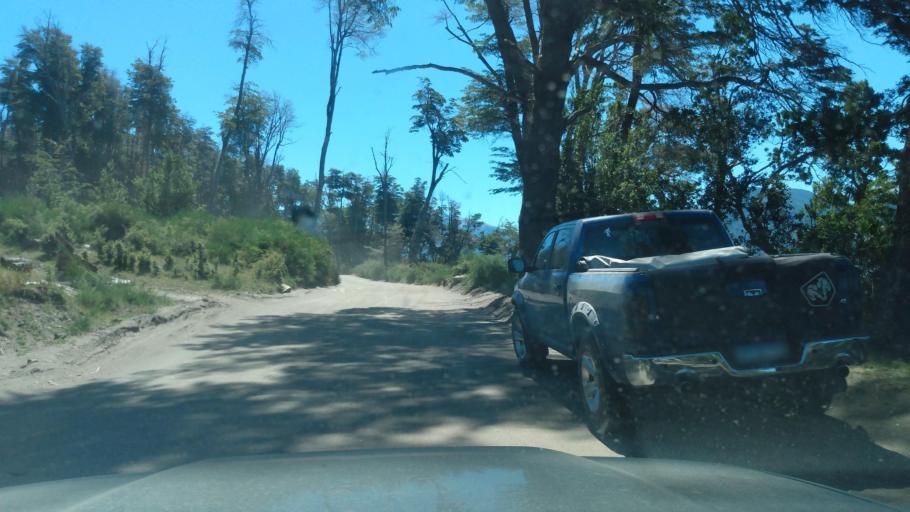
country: AR
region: Neuquen
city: Villa La Angostura
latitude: -40.6450
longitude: -71.4394
